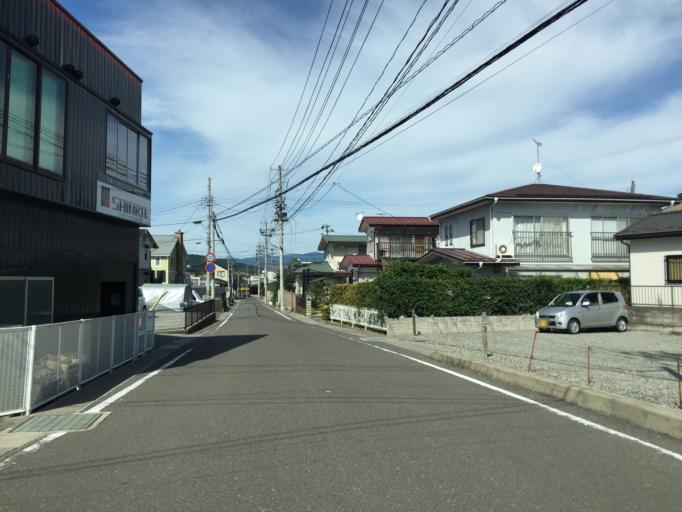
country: JP
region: Fukushima
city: Fukushima-shi
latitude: 37.7500
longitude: 140.4847
